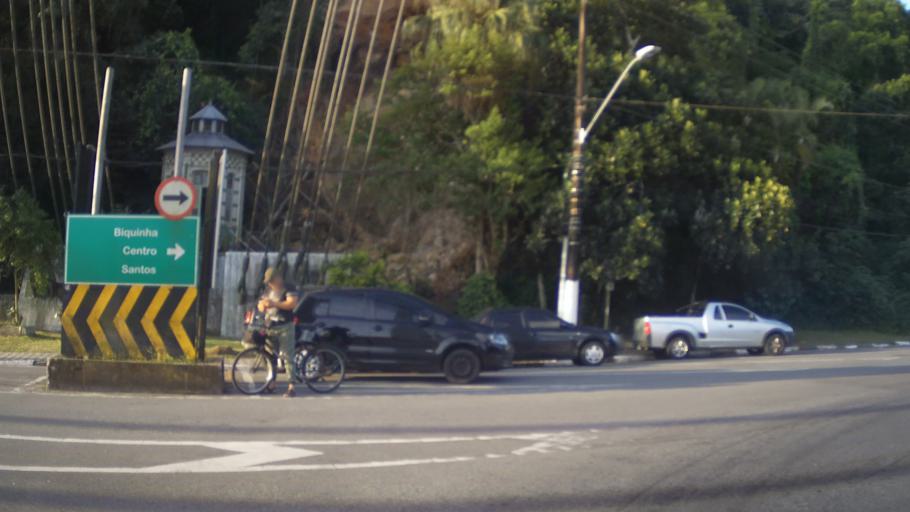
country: BR
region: Sao Paulo
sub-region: Sao Vicente
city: Sao Vicente
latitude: -23.9747
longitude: -46.3888
